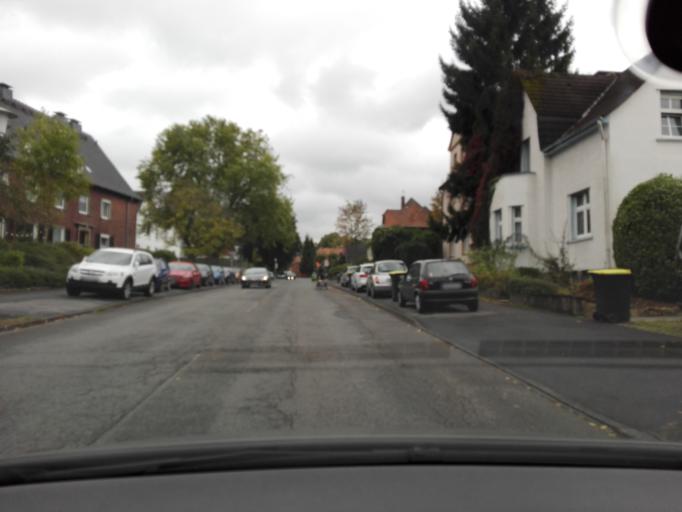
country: DE
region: North Rhine-Westphalia
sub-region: Regierungsbezirk Arnsberg
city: Unna
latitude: 51.5367
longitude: 7.6751
